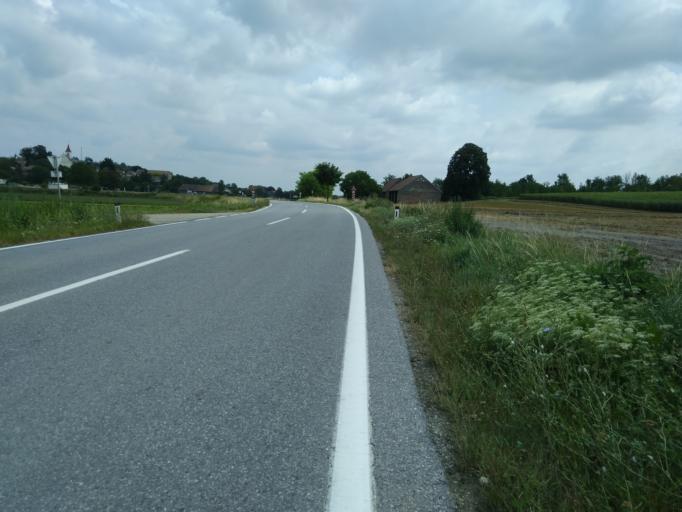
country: AT
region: Lower Austria
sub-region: Politischer Bezirk Ganserndorf
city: Gross-Schweinbarth
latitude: 48.3963
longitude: 16.6487
